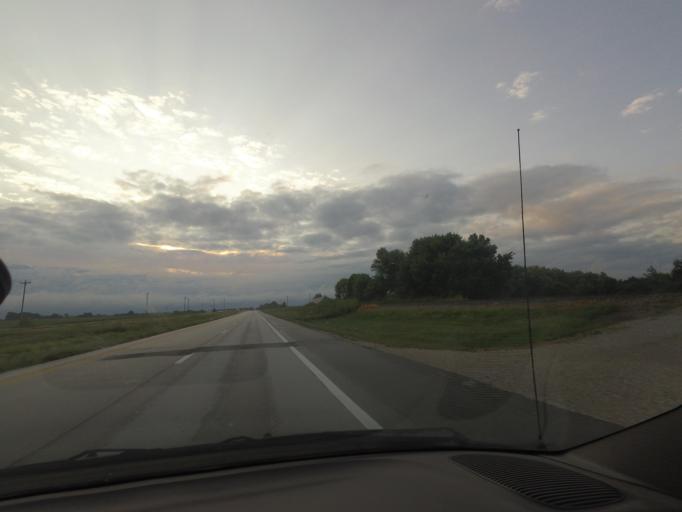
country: US
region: Missouri
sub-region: Shelby County
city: Shelbina
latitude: 39.7021
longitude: -92.0758
